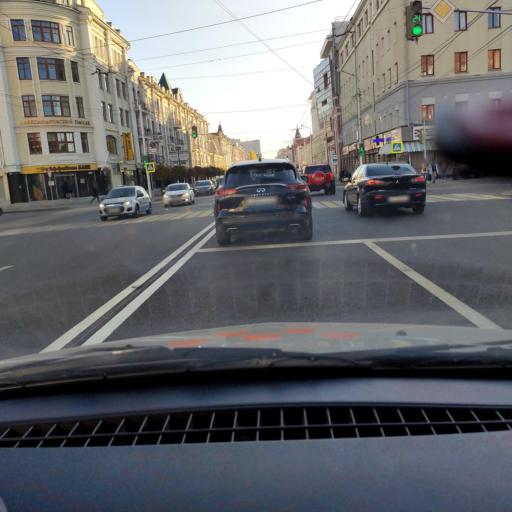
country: RU
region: Bashkortostan
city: Ufa
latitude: 54.7298
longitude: 55.9428
